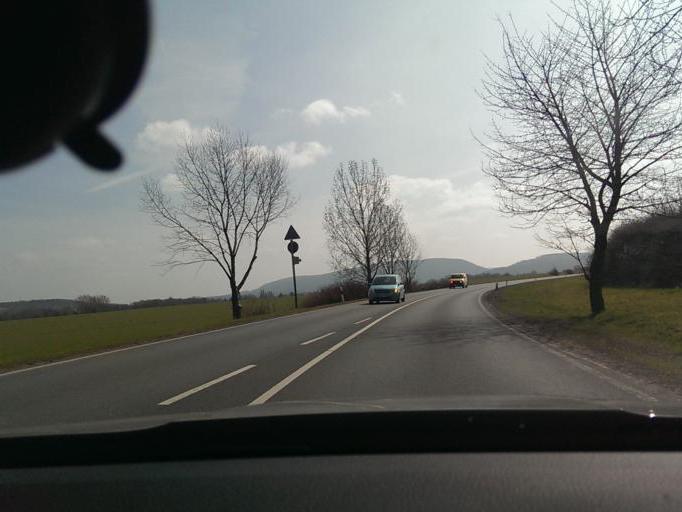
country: DE
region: Thuringia
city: Hohenkirchen
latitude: 50.8376
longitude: 10.7212
